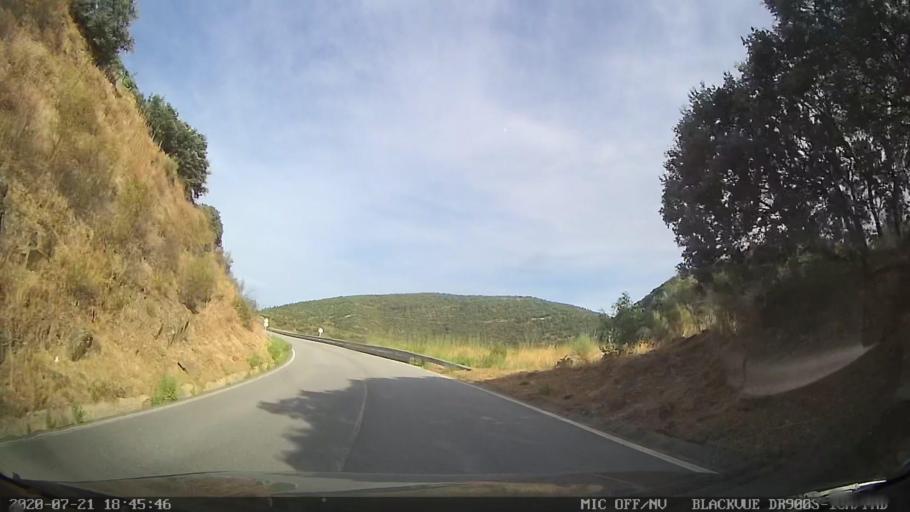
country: PT
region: Viseu
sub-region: Sao Joao da Pesqueira
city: Sao Joao da Pesqueira
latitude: 41.1194
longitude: -7.4491
